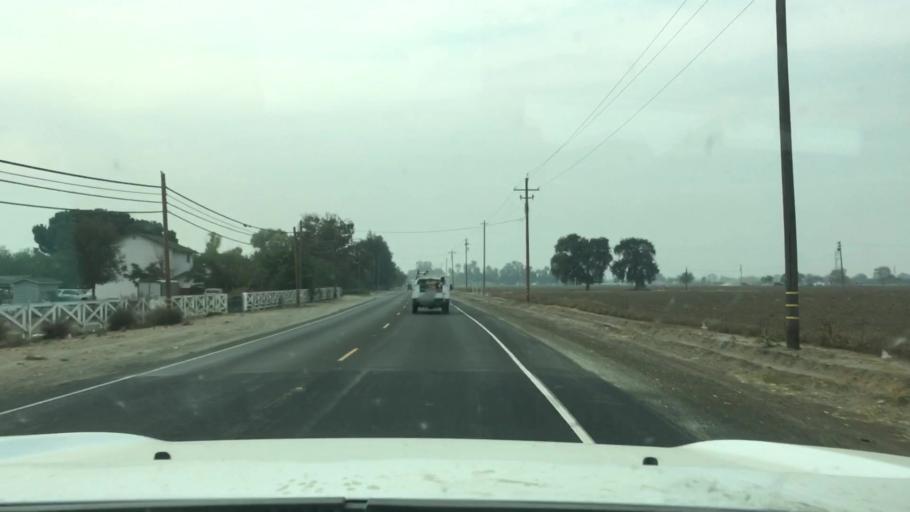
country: US
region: California
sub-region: San Joaquin County
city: French Camp
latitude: 37.8676
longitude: -121.2418
